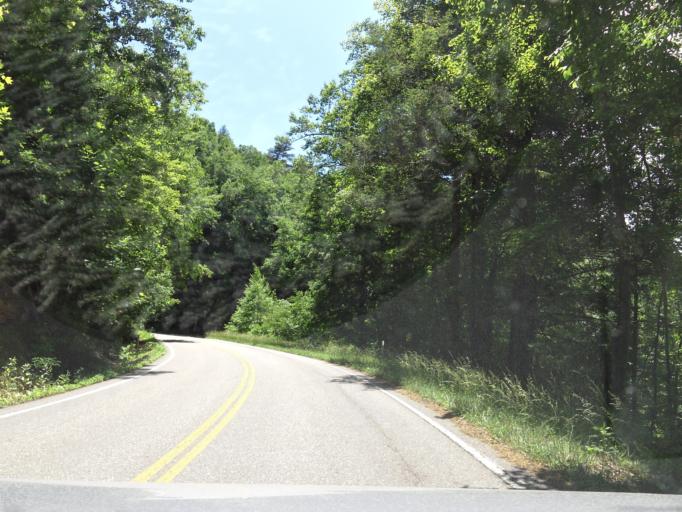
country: US
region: North Carolina
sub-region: Graham County
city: Robbinsville
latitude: 35.5048
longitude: -83.9485
